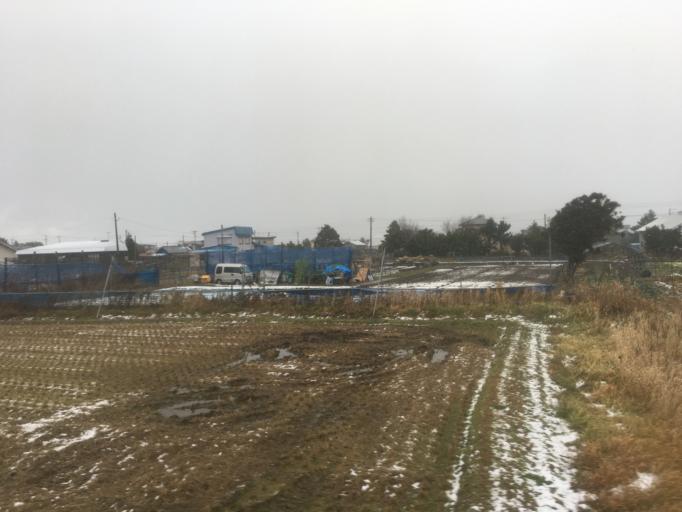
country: JP
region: Aomori
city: Aomori Shi
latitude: 40.9148
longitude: 140.6673
